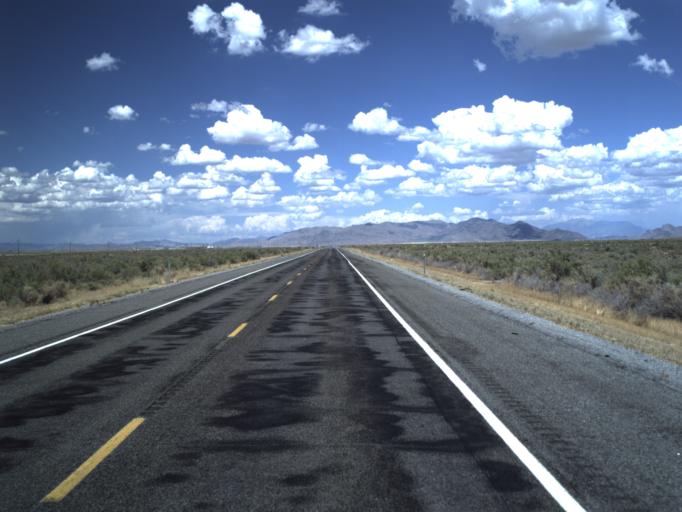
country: US
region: Utah
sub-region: Millard County
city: Delta
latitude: 39.4344
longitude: -112.4623
